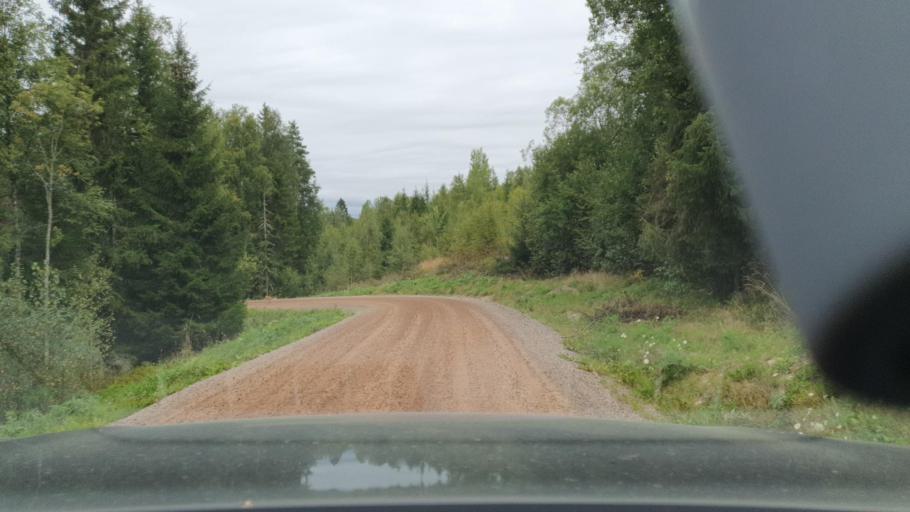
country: SE
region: Vaermland
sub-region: Eda Kommun
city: Charlottenberg
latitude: 60.0901
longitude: 12.5044
